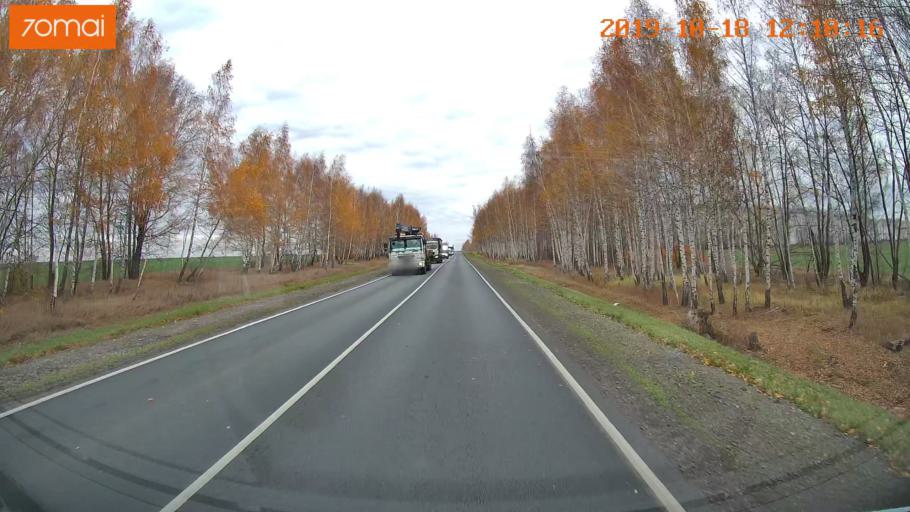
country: RU
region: Rjazan
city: Zakharovo
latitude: 54.3908
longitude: 39.3272
